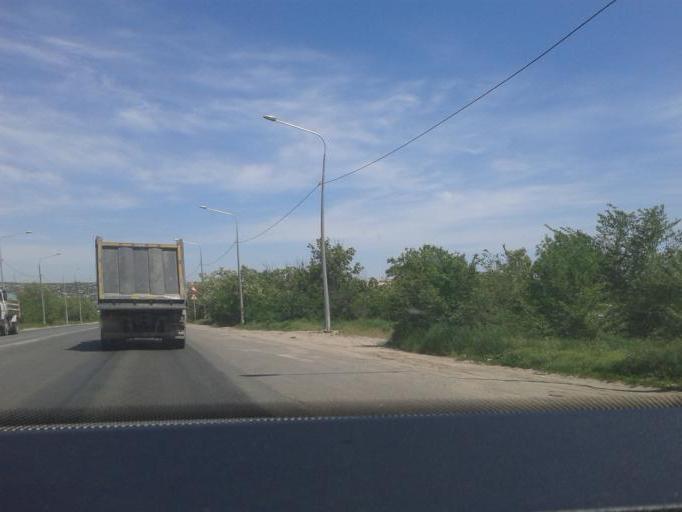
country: RU
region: Volgograd
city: Gorodishche
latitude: 48.7898
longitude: 44.5206
